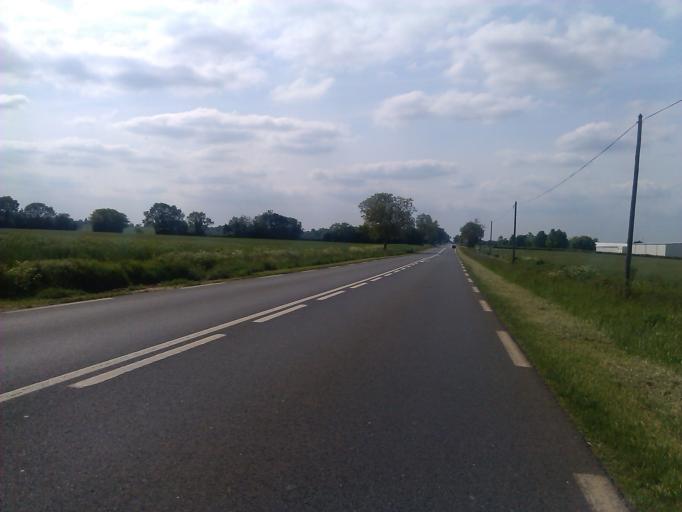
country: FR
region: Centre
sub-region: Departement de l'Indre
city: La Chatre
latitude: 46.5708
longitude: 2.0272
